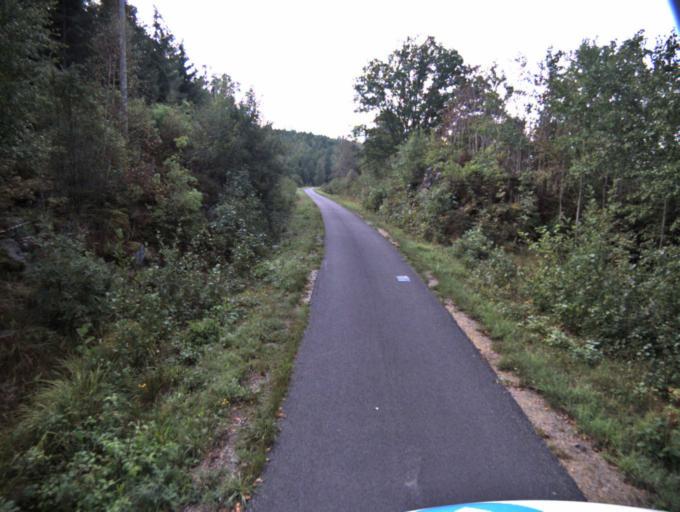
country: SE
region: Vaestra Goetaland
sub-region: Ulricehamns Kommun
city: Ulricehamn
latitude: 57.7026
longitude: 13.3940
